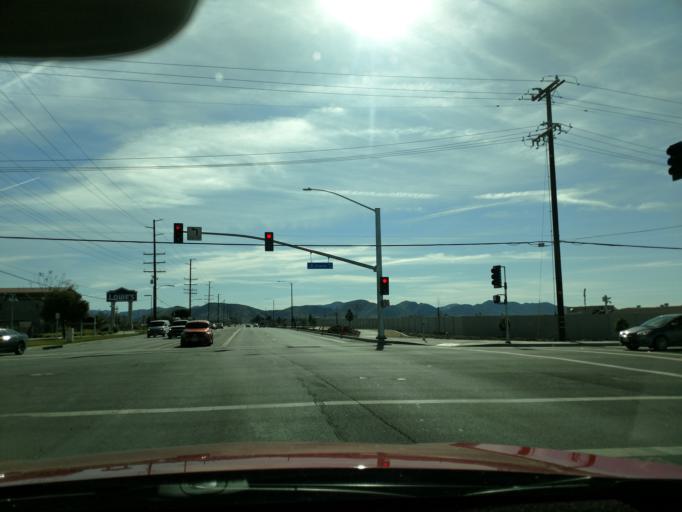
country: US
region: California
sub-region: Riverside County
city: Hemet
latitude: 33.7441
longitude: -117.0067
